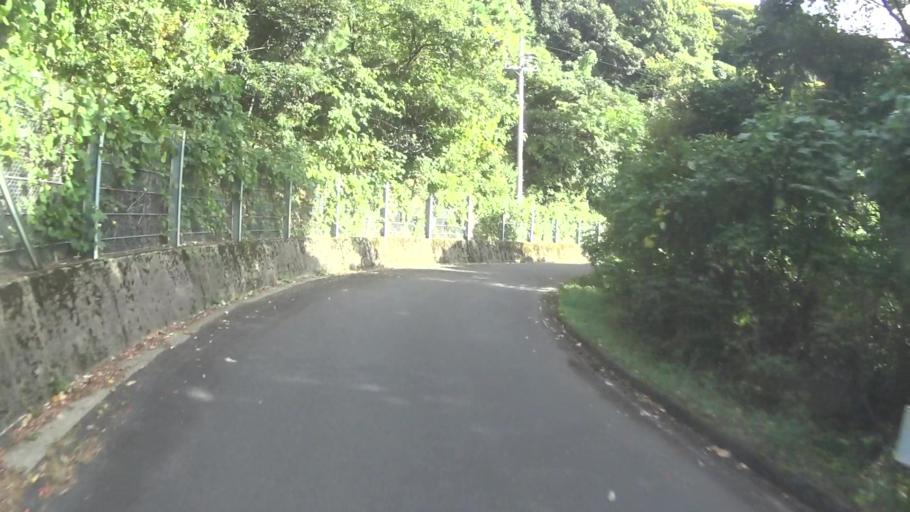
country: JP
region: Kyoto
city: Maizuru
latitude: 35.5627
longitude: 135.4075
